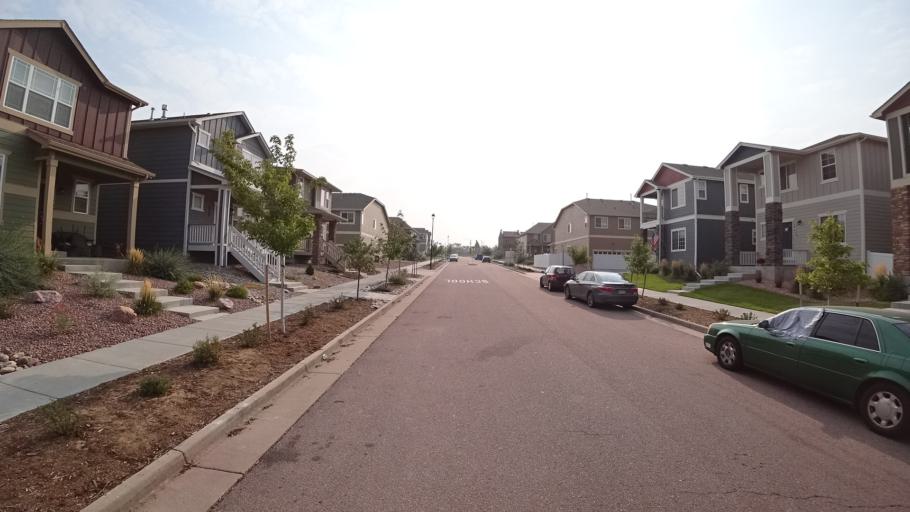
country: US
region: Colorado
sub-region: El Paso County
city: Stratmoor
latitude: 38.8108
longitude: -104.7829
